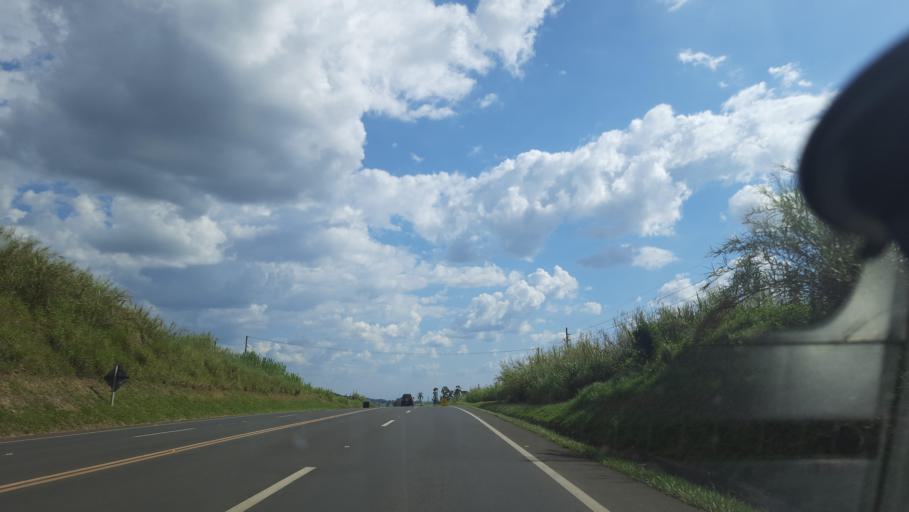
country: BR
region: Sao Paulo
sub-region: Sao Jose Do Rio Pardo
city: Sao Jose do Rio Pardo
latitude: -21.6581
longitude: -46.9160
